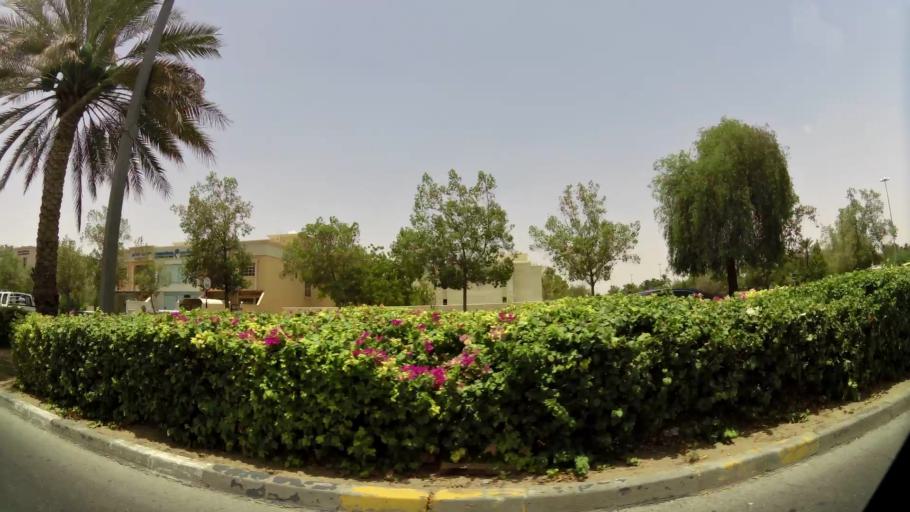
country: AE
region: Abu Dhabi
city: Al Ain
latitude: 24.2122
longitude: 55.7462
